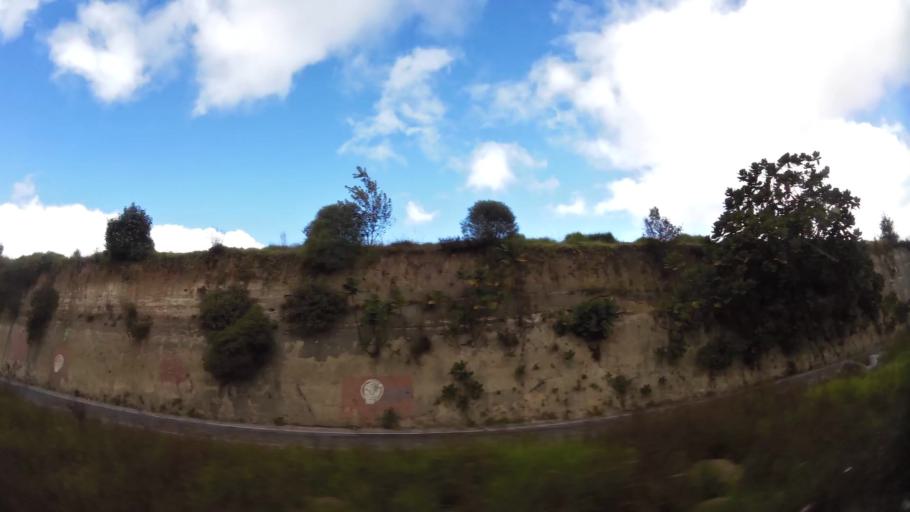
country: GT
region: Quetzaltenango
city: Salcaja
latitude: 14.8760
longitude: -91.4717
